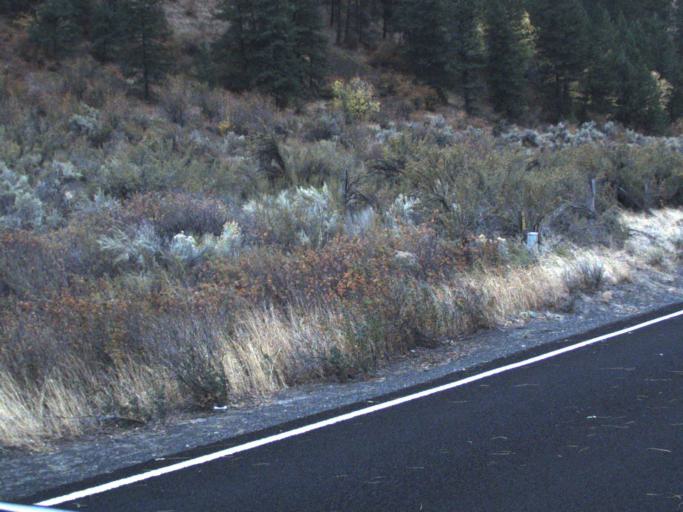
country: US
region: Washington
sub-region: Okanogan County
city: Coulee Dam
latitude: 47.8989
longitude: -118.7053
